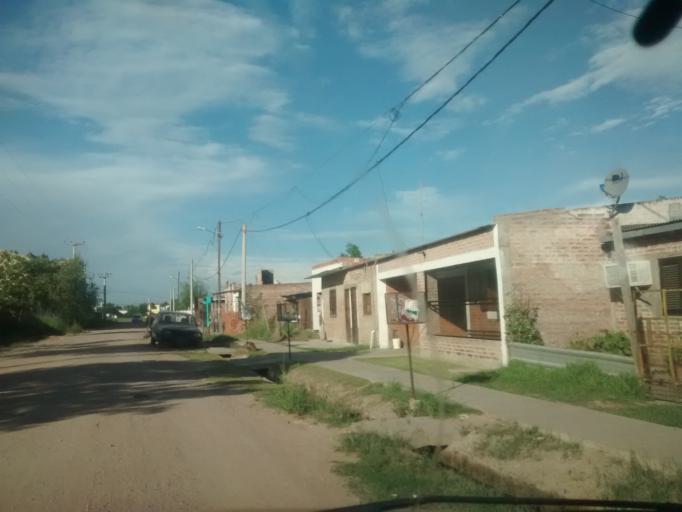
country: AR
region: Chaco
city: Fontana
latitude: -27.4554
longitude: -59.0282
